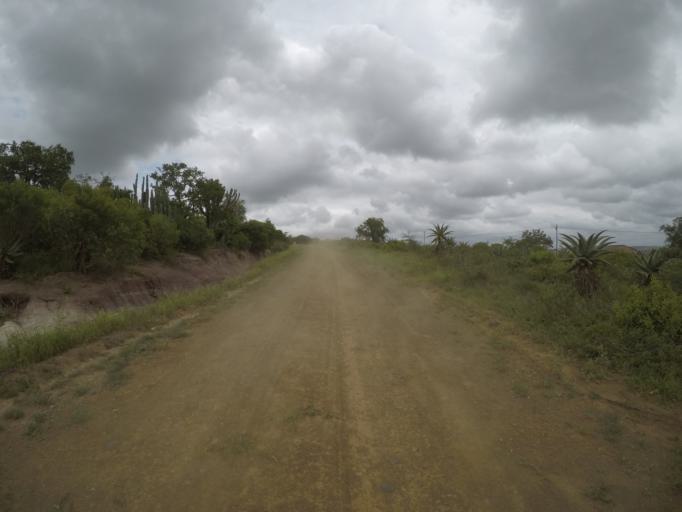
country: ZA
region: KwaZulu-Natal
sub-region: uThungulu District Municipality
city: Empangeni
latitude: -28.5821
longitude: 31.8657
